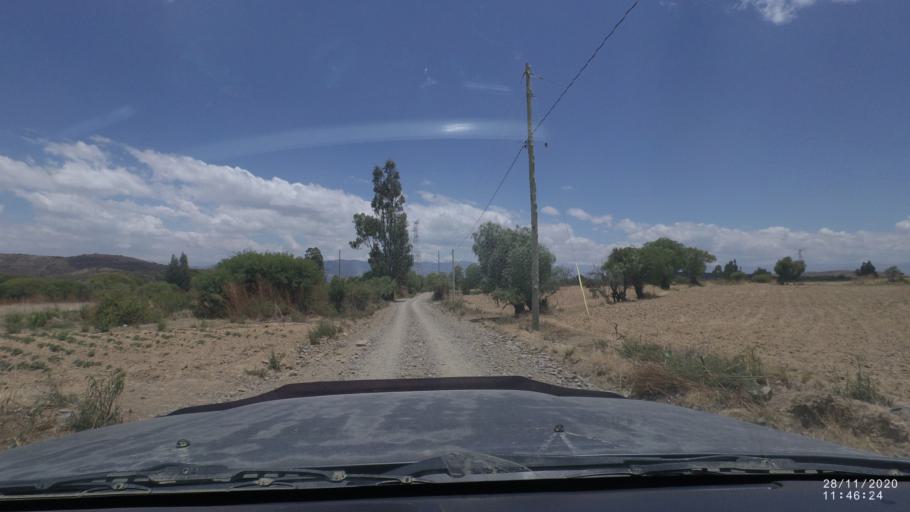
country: BO
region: Cochabamba
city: Tarata
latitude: -17.6511
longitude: -66.0429
